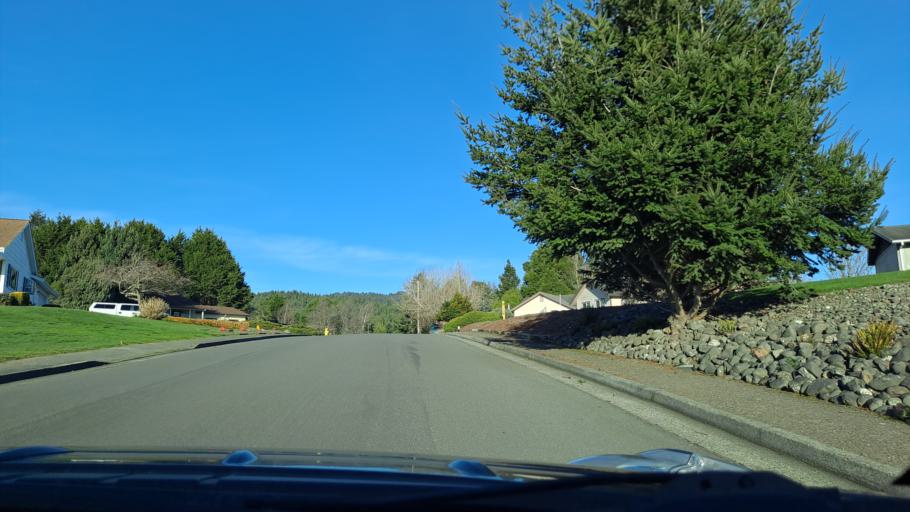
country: US
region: California
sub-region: Humboldt County
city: Fortuna
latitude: 40.5950
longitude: -124.1377
